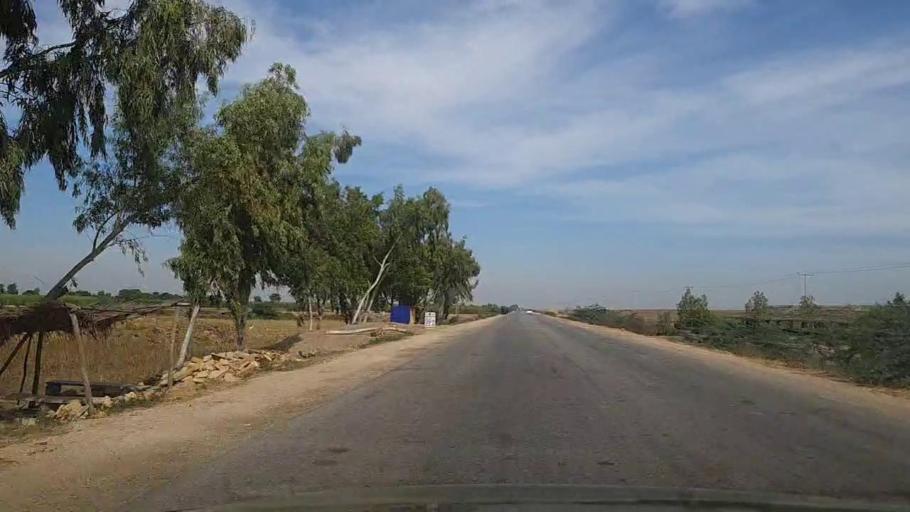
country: PK
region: Sindh
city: Daro Mehar
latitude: 24.9409
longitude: 68.1092
